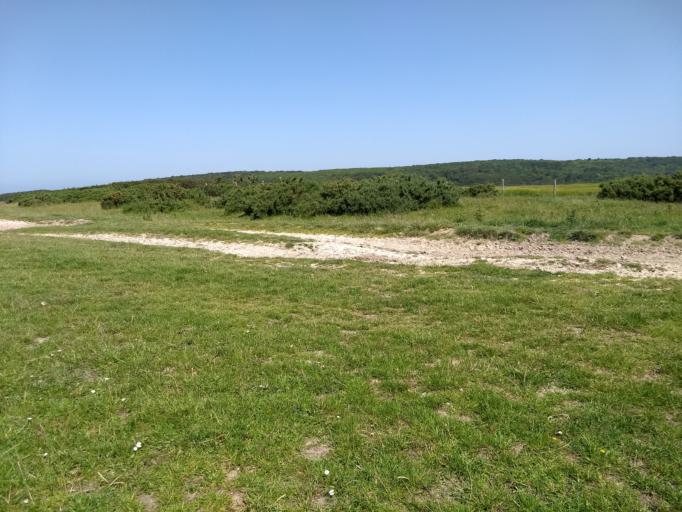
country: GB
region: England
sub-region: Isle of Wight
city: Shalfleet
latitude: 50.6517
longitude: -1.3823
